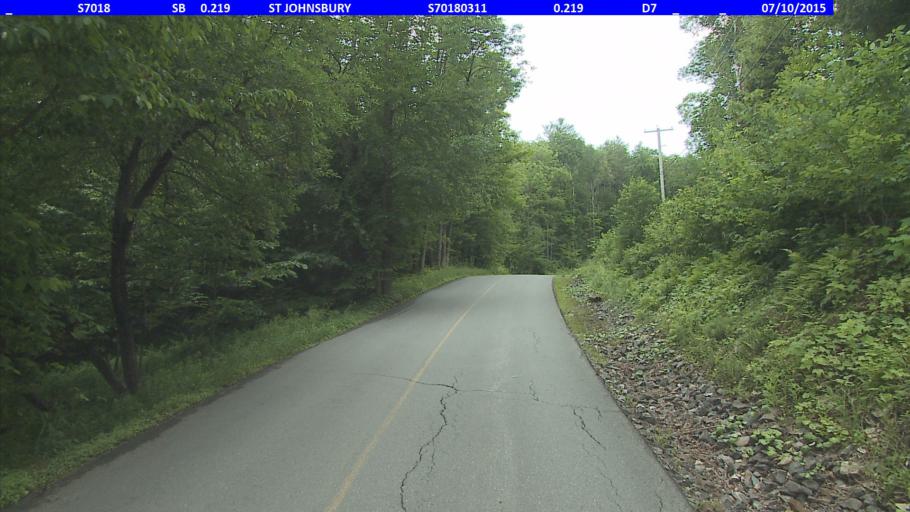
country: US
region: Vermont
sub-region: Caledonia County
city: Saint Johnsbury
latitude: 44.4150
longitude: -71.9895
